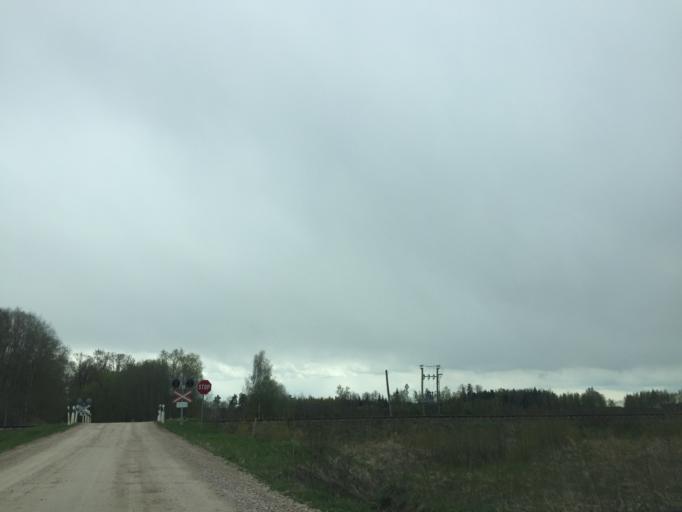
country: LV
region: Lecava
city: Iecava
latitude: 56.6357
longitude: 24.1835
